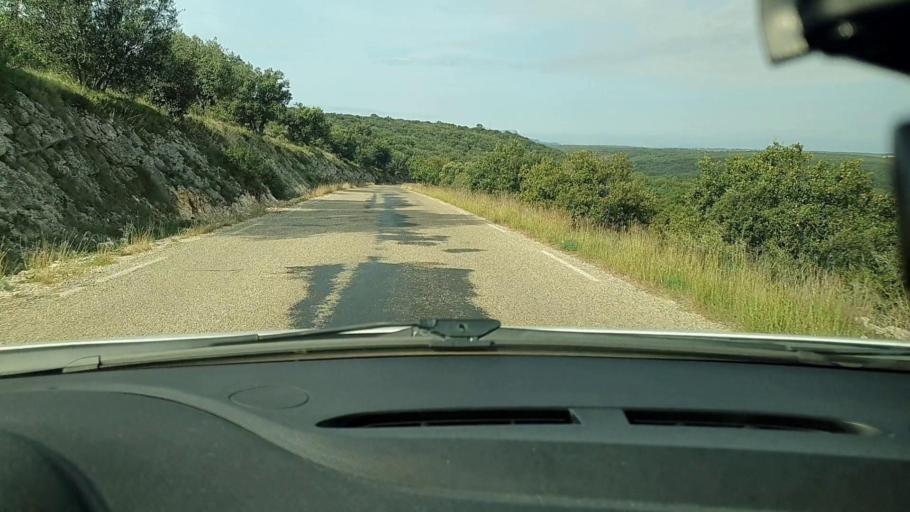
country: FR
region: Languedoc-Roussillon
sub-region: Departement du Gard
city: Saint-Quentin-la-Poterie
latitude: 44.1266
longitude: 4.4110
